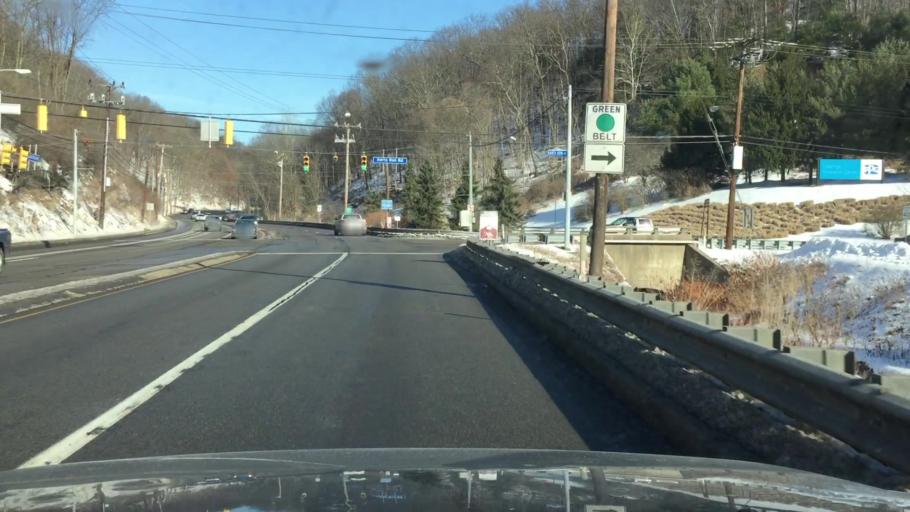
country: US
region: Pennsylvania
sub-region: Allegheny County
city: Allison Park
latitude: 40.5693
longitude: -79.9541
